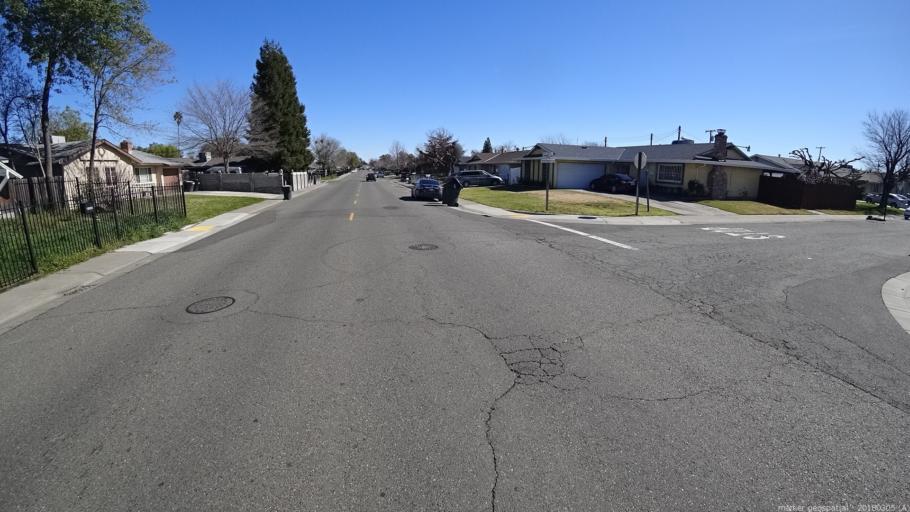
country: US
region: California
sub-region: Sacramento County
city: Florin
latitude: 38.4990
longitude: -121.4231
